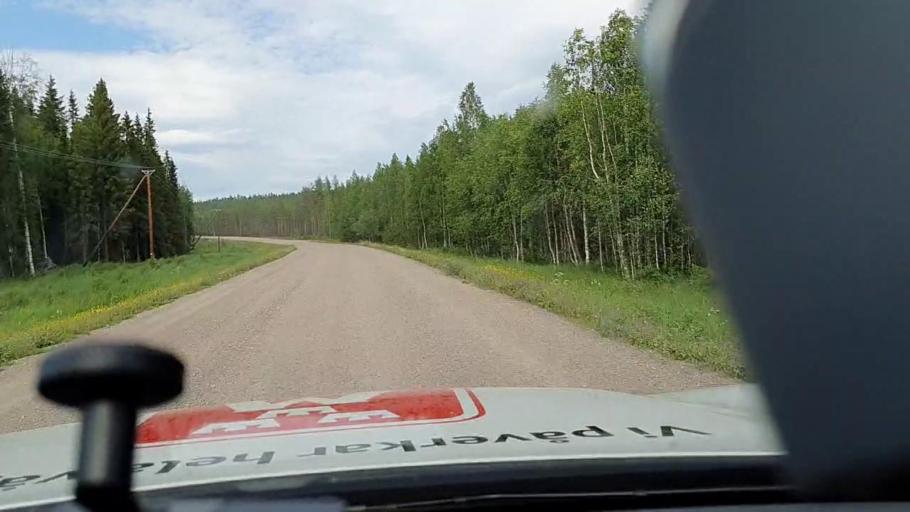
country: SE
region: Norrbotten
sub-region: Alvsbyns Kommun
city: AElvsbyn
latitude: 66.1206
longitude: 20.9877
